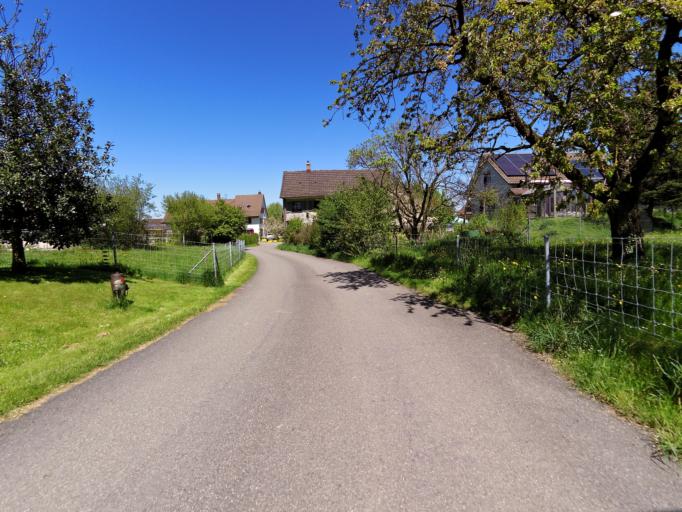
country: CH
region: Thurgau
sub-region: Weinfelden District
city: Berg
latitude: 47.6132
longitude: 9.1680
